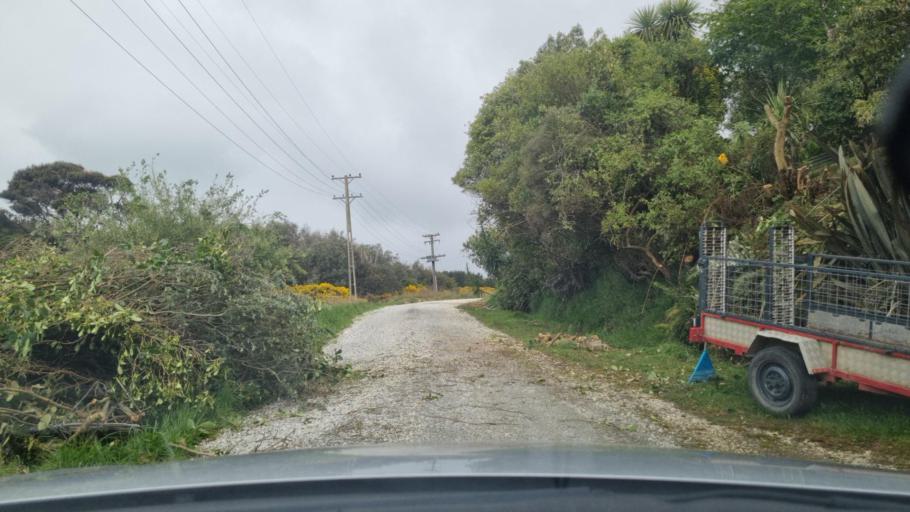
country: NZ
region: Southland
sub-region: Invercargill City
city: Bluff
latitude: -46.5763
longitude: 168.2981
